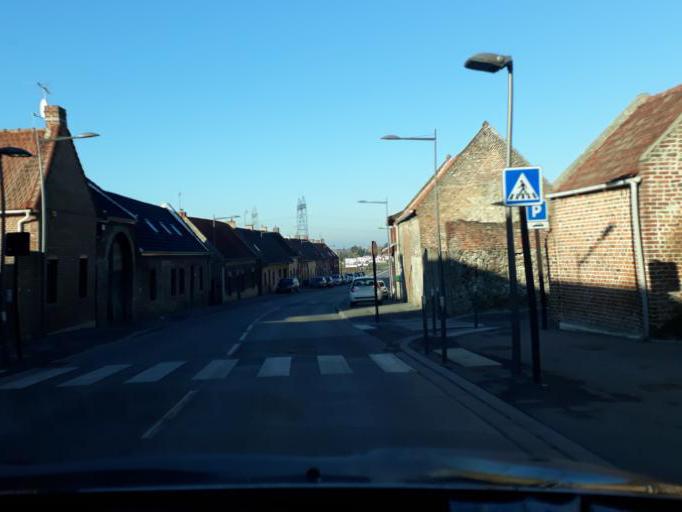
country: FR
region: Nord-Pas-de-Calais
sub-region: Departement du Nord
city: Lewarde
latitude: 50.3415
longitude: 3.1633
